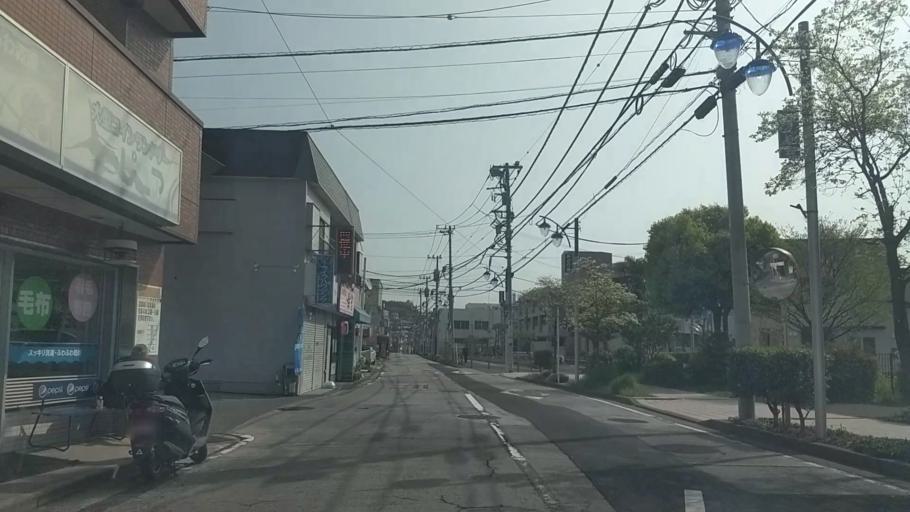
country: JP
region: Kanagawa
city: Yokohama
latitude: 35.3655
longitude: 139.6220
